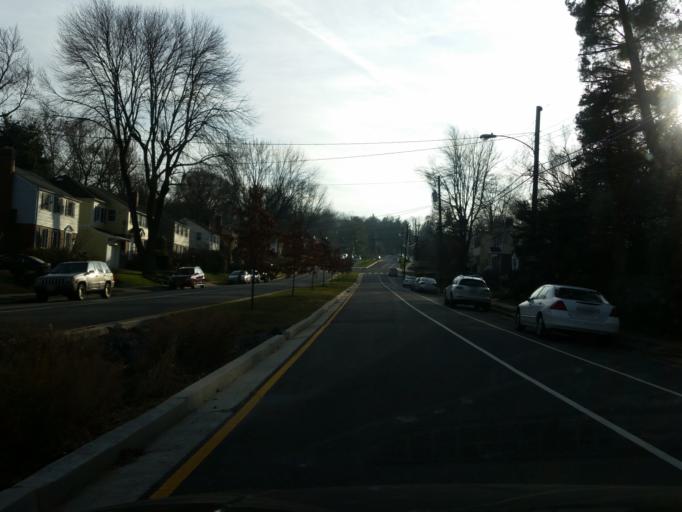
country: US
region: Virginia
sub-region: Fairfax County
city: Seven Corners
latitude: 38.8764
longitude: -77.1421
